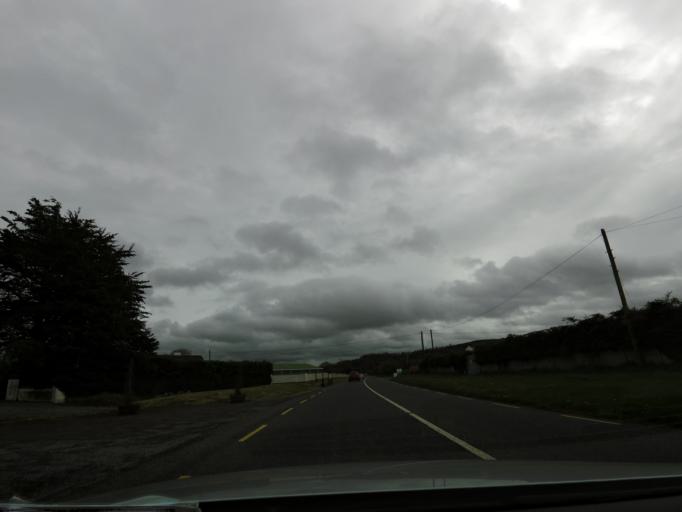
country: IE
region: Leinster
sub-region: Kilkenny
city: Ballyragget
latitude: 52.7289
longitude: -7.3796
